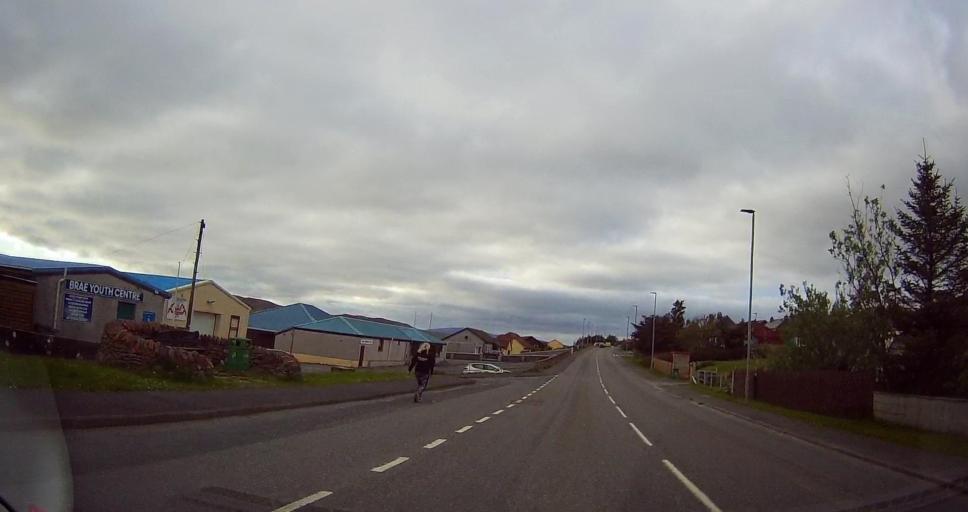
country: GB
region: Scotland
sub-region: Shetland Islands
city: Lerwick
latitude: 60.3887
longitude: -1.3486
